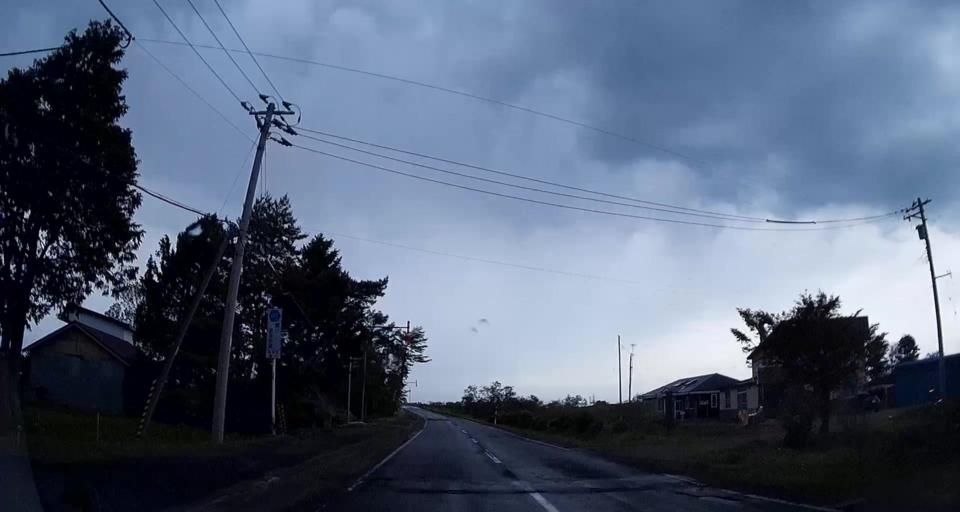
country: JP
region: Hokkaido
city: Chitose
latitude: 42.6972
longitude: 141.8470
